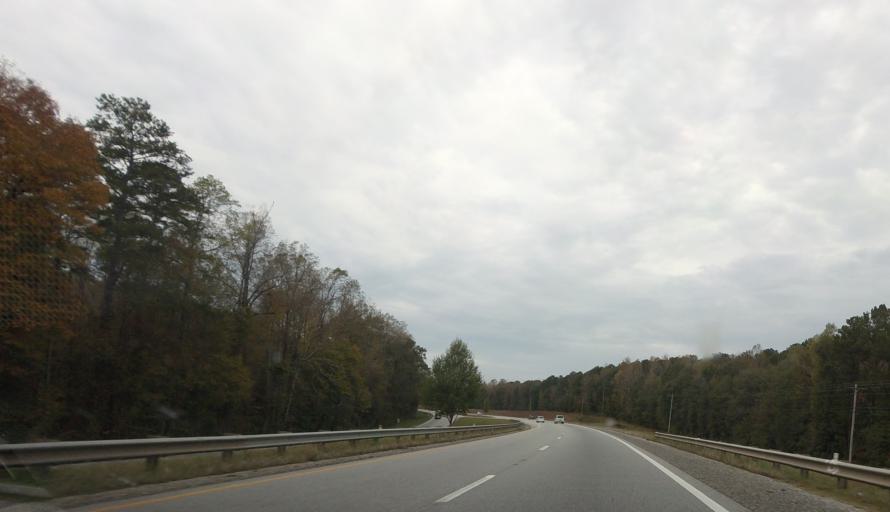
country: US
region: Alabama
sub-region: Lee County
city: Opelika
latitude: 32.6335
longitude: -85.2863
